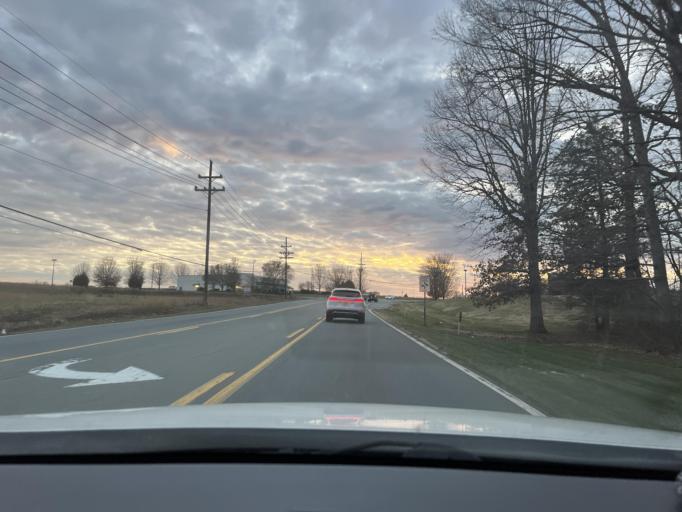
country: US
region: North Carolina
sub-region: Guilford County
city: Gibsonville
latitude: 36.0635
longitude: -79.6010
